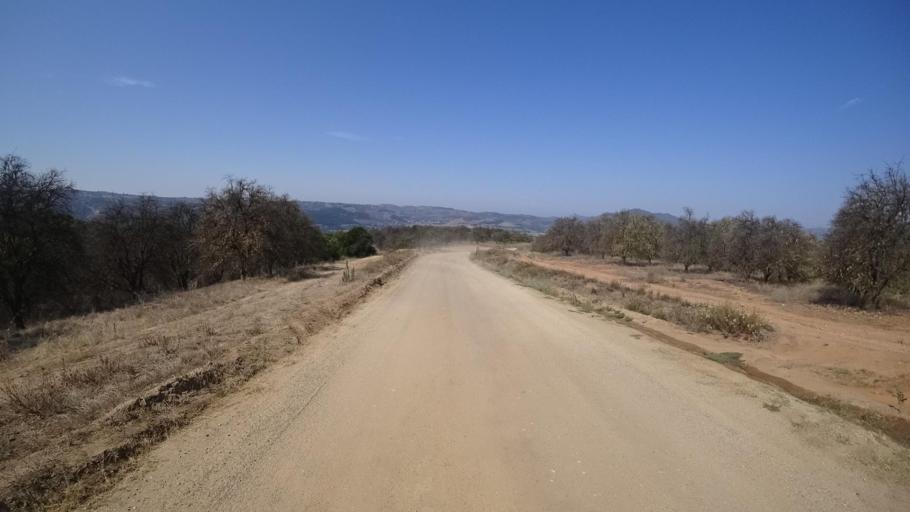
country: US
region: California
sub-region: San Diego County
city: Valley Center
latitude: 33.3230
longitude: -116.9717
